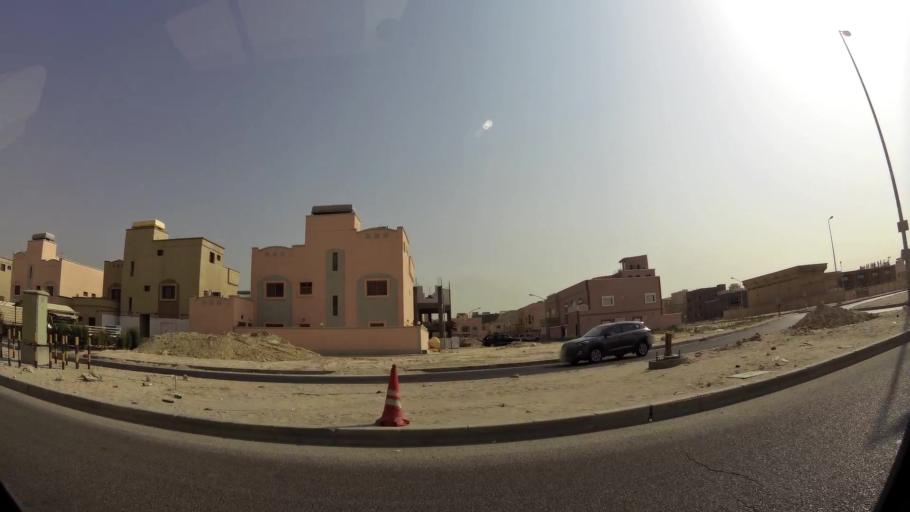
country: KW
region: Muhafazat al Jahra'
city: Al Jahra'
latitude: 29.3549
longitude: 47.7567
